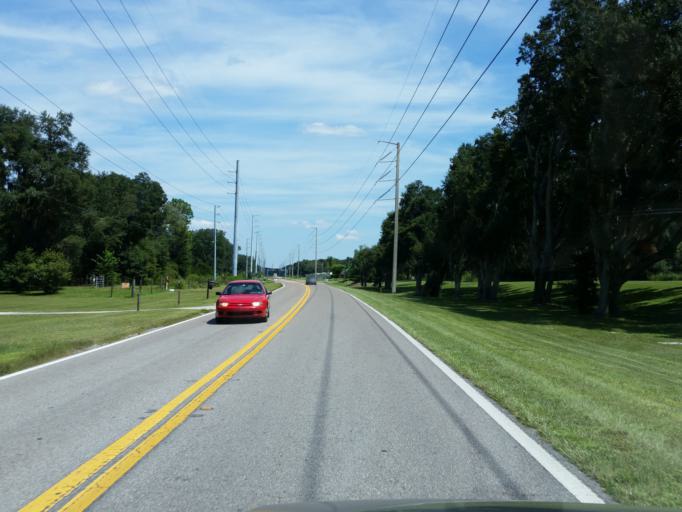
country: US
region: Florida
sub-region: Pasco County
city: Zephyrhills North
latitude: 28.2526
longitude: -82.1379
